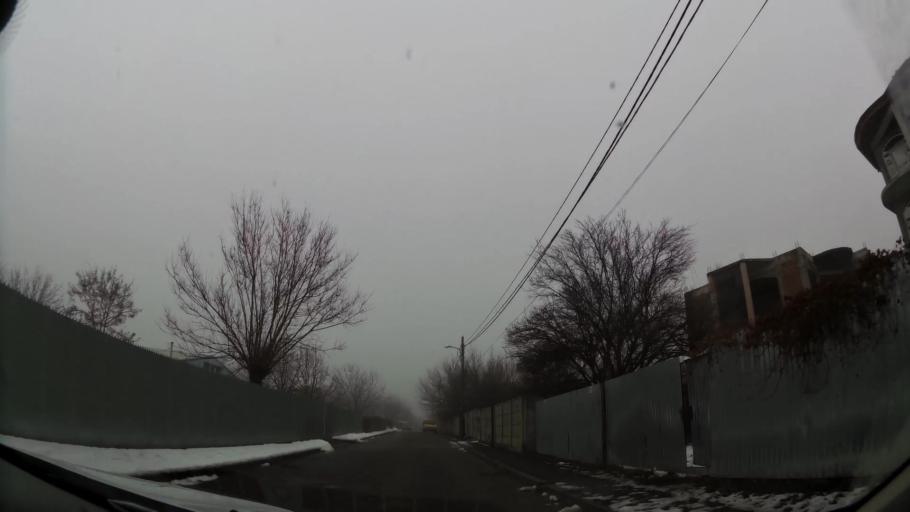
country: RO
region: Ilfov
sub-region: Comuna Chiajna
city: Rosu
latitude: 44.4726
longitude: 26.0077
